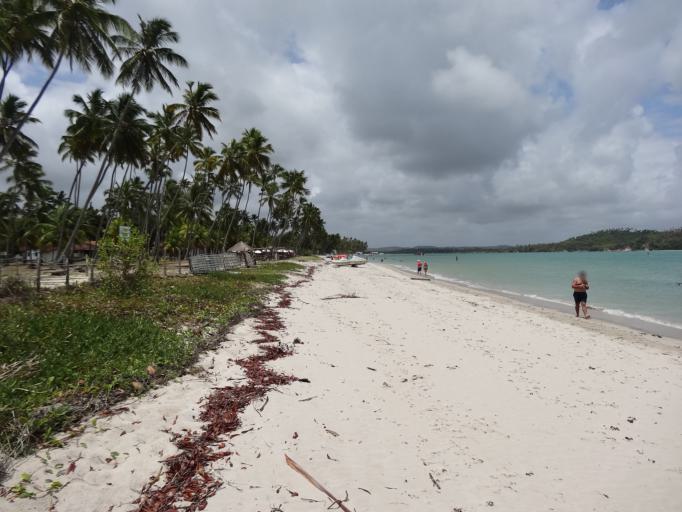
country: BR
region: Pernambuco
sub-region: Tamandare
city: Tamandare
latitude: -8.6986
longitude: -35.0861
